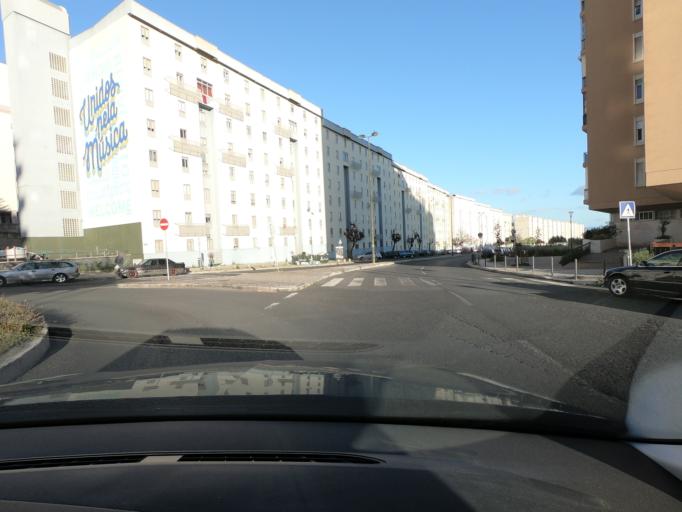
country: PT
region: Lisbon
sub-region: Lisbon
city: Lisbon
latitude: 38.7278
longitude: -9.1241
